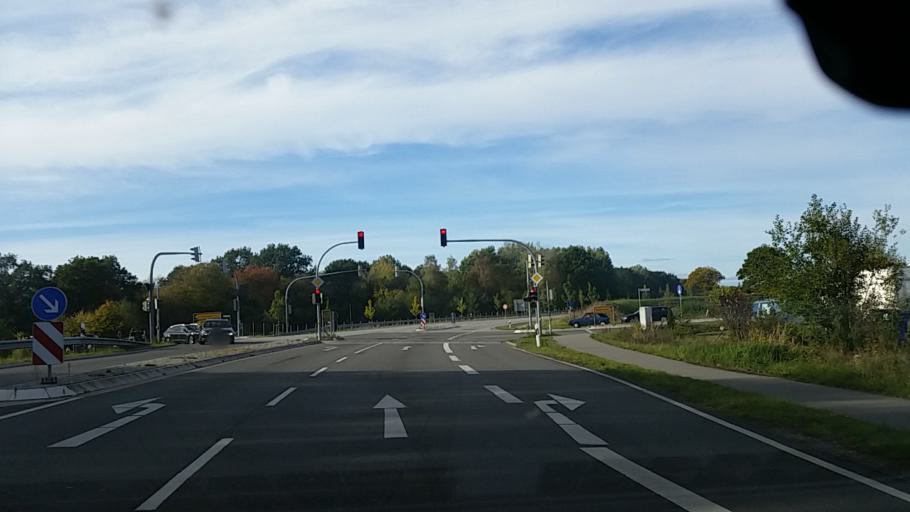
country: DE
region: Schleswig-Holstein
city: Delingsdorf
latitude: 53.7238
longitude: 10.2422
